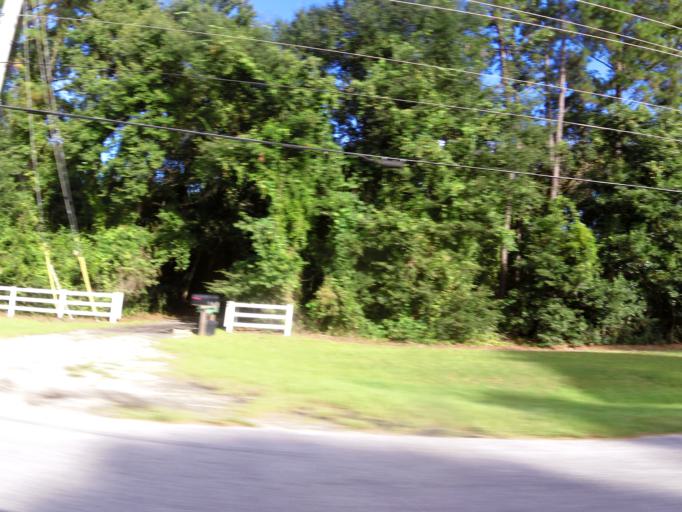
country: US
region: Georgia
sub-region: Glynn County
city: Country Club Estates
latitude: 31.2545
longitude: -81.4429
